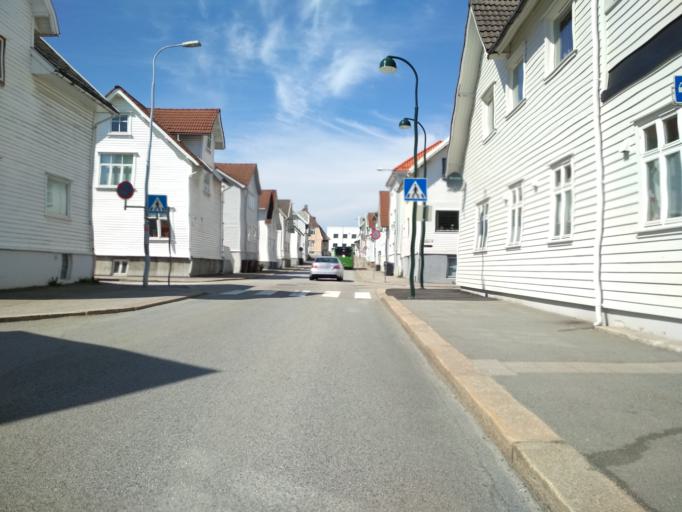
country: NO
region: Rogaland
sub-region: Stavanger
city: Stavanger
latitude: 58.9696
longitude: 5.7219
